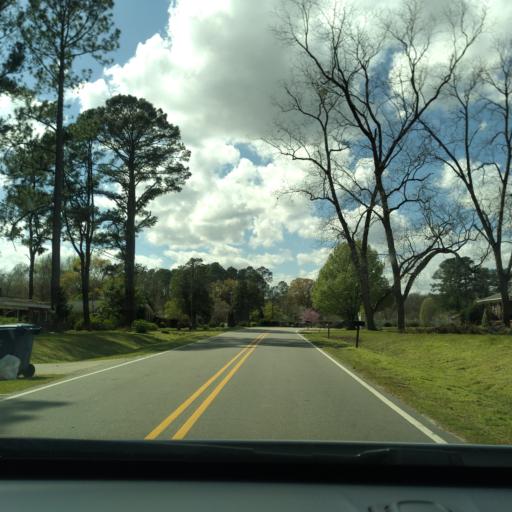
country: US
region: North Carolina
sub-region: Washington County
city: Plymouth
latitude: 35.8506
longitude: -76.7338
